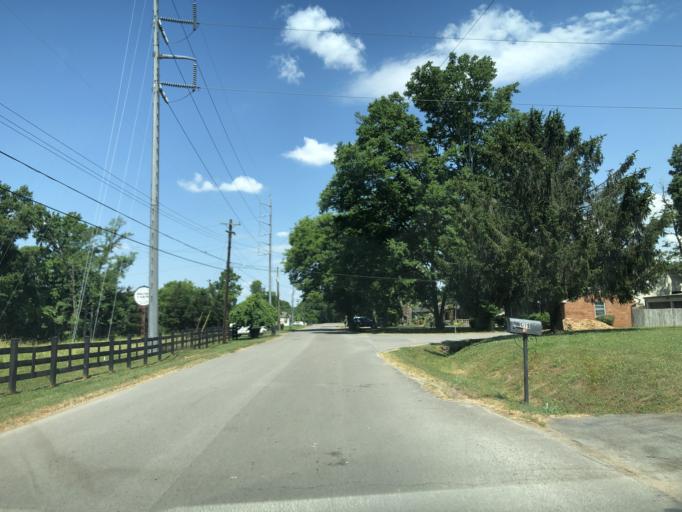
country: US
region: Tennessee
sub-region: Davidson County
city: Lakewood
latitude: 36.2787
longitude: -86.6752
